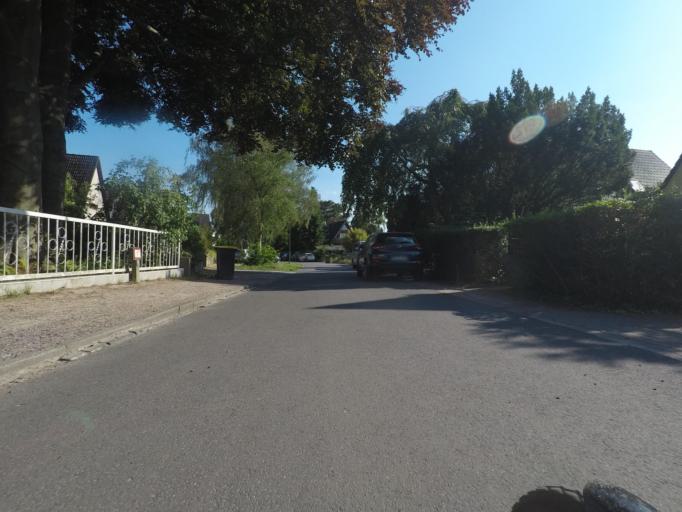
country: DE
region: Hamburg
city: Wellingsbuettel
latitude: 53.6200
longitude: 10.0920
